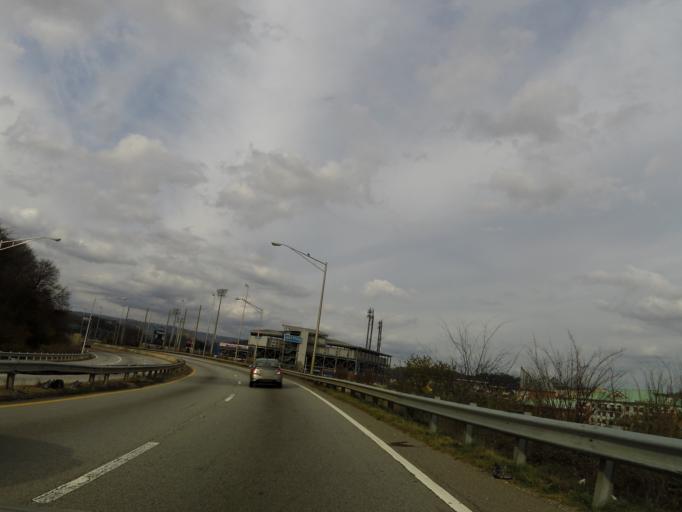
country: US
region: Tennessee
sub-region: Hamilton County
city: Chattanooga
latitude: 35.0518
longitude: -85.3138
